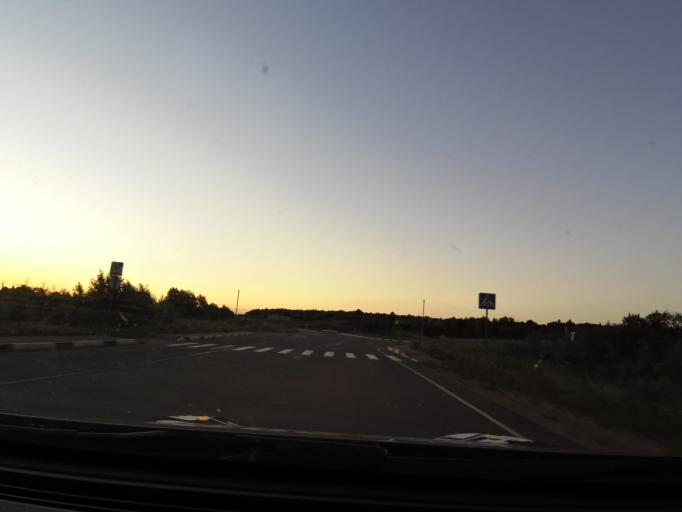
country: RU
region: Vologda
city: Vytegra
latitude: 60.9267
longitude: 36.0904
